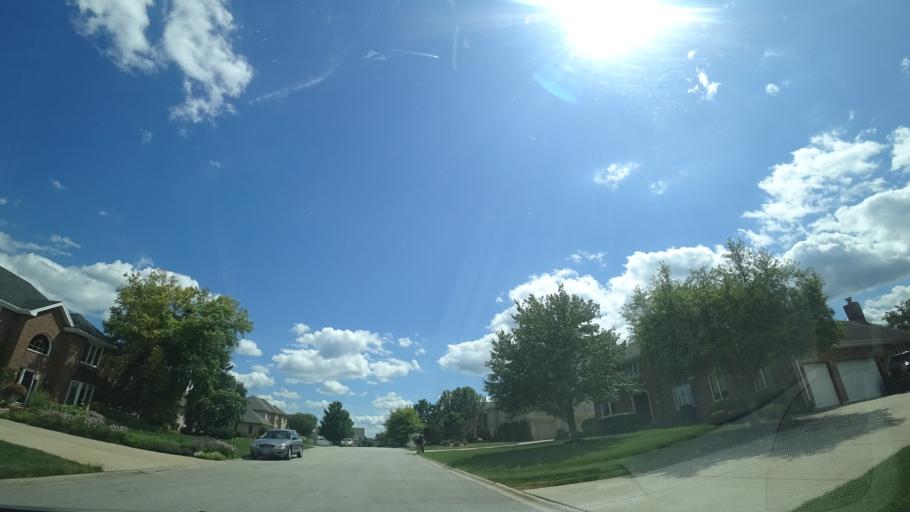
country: US
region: Illinois
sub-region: Will County
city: Homer Glen
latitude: 41.5830
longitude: -87.9126
